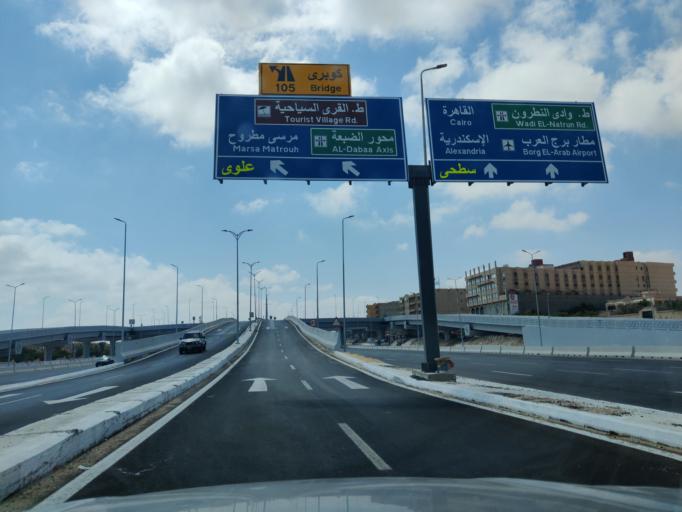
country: EG
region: Muhafazat Matruh
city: Al `Alamayn
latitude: 30.8403
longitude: 28.9512
